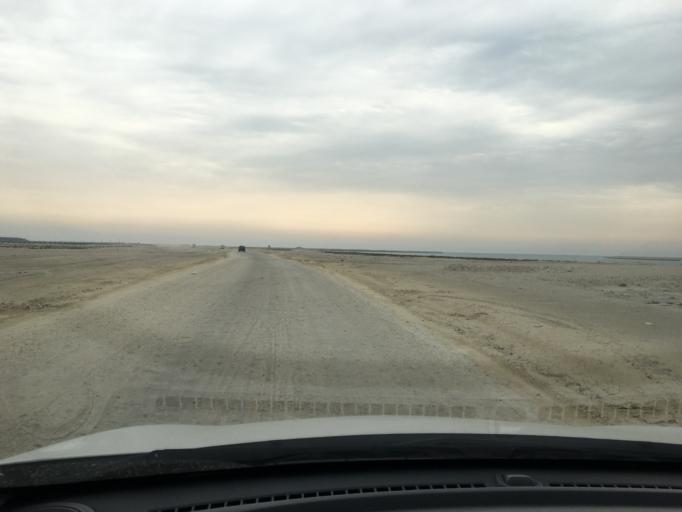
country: BH
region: Central Governorate
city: Dar Kulayb
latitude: 25.8334
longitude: 50.5931
